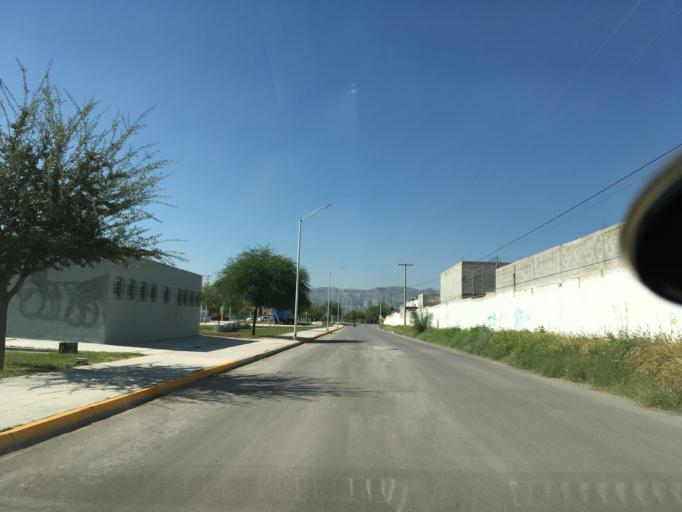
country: MX
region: Coahuila
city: Torreon
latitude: 25.5233
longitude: -103.3785
